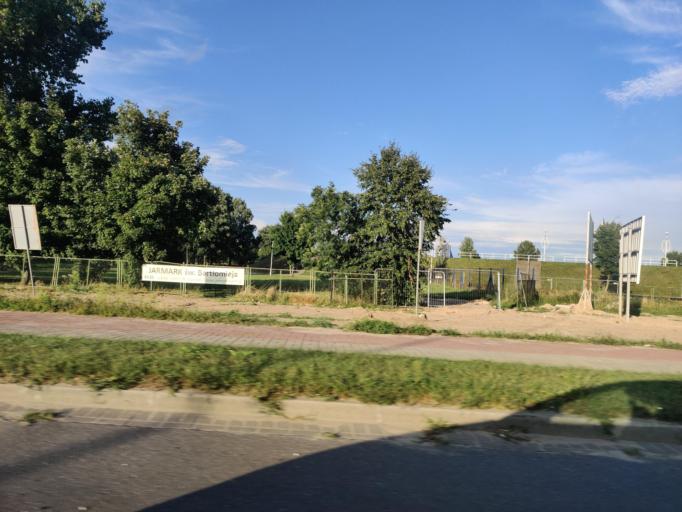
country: PL
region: Greater Poland Voivodeship
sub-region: Konin
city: Konin
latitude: 52.2188
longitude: 18.2530
